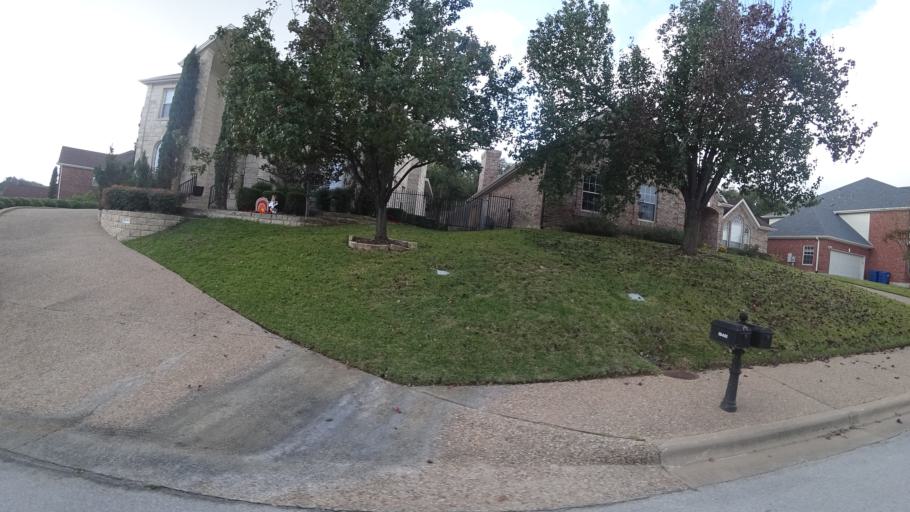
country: US
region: Texas
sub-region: Travis County
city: Barton Creek
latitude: 30.3110
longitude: -97.8953
